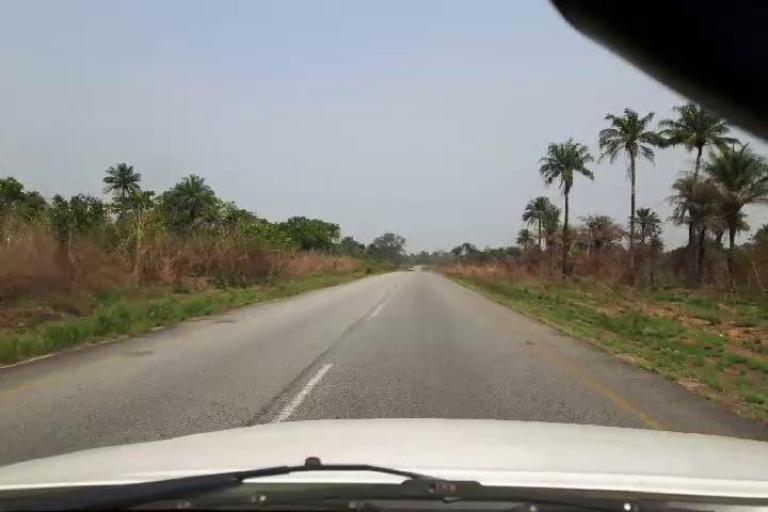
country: SL
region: Southern Province
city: Largo
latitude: 8.3075
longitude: -12.2072
